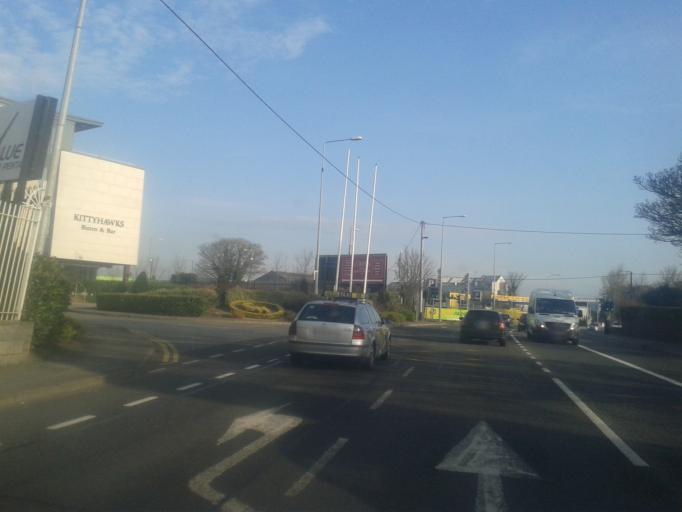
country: IE
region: Leinster
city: Beaumont
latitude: 53.4149
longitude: -6.2392
